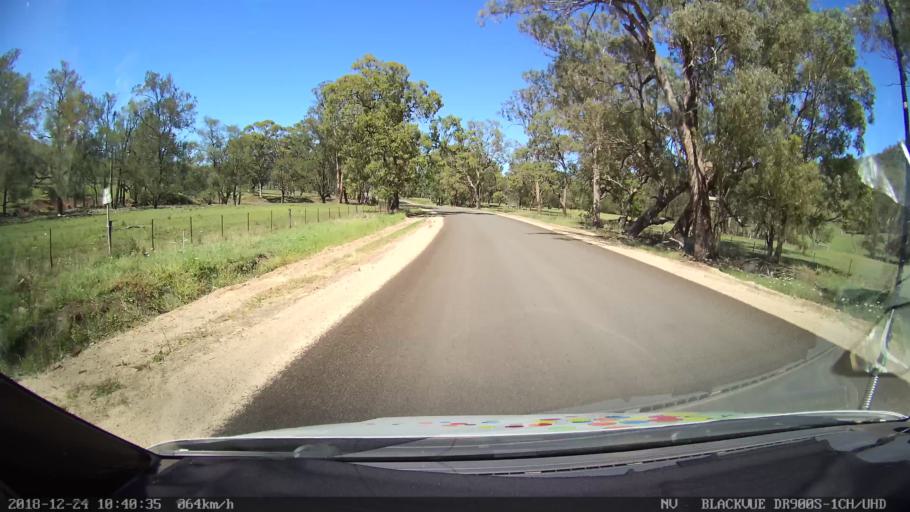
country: AU
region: New South Wales
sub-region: Upper Hunter Shire
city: Merriwa
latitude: -31.8626
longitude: 150.4660
